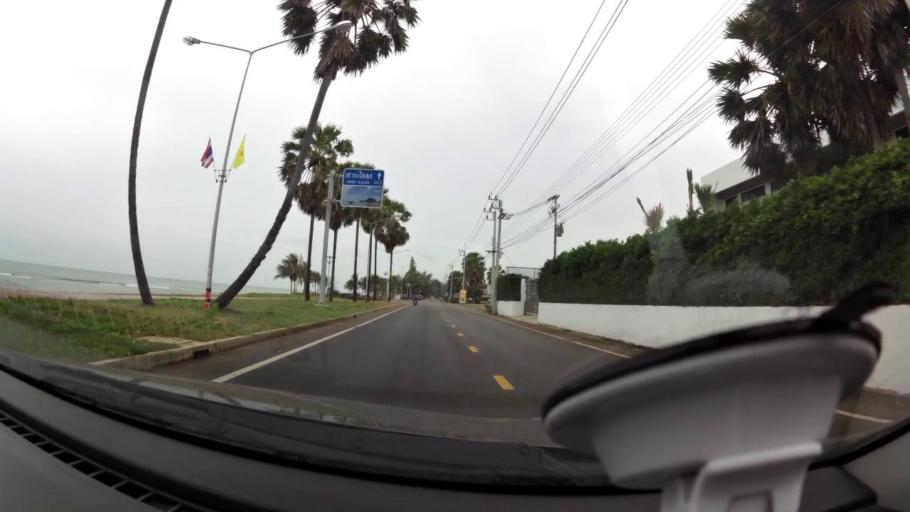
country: TH
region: Prachuap Khiri Khan
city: Pran Buri
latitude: 12.3723
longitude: 100.0000
